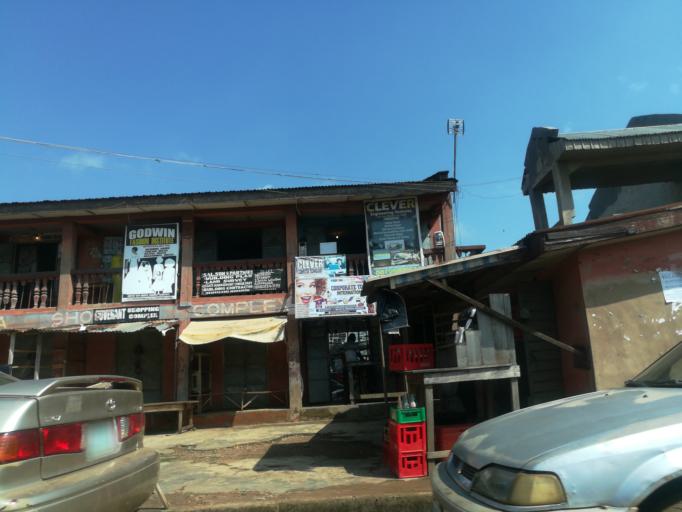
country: NG
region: Oyo
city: Ibadan
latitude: 7.4213
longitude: 3.9771
